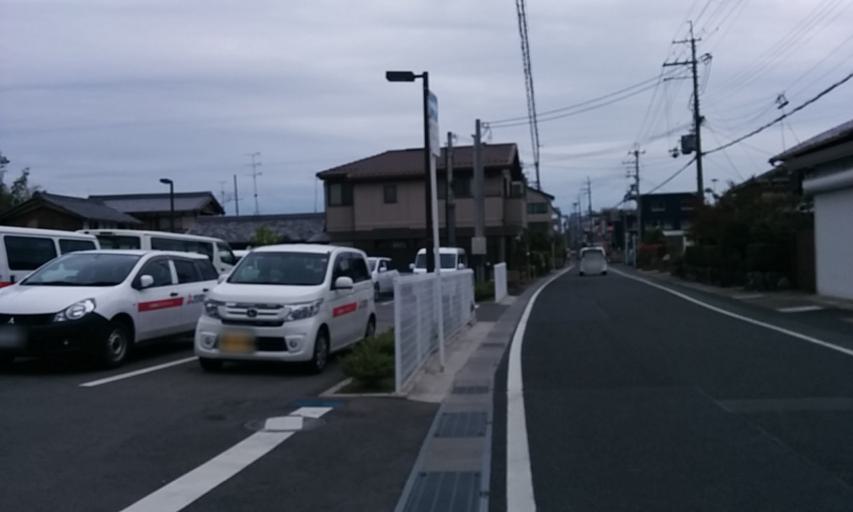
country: JP
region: Shiga Prefecture
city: Kusatsu
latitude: 35.0063
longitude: 135.9530
